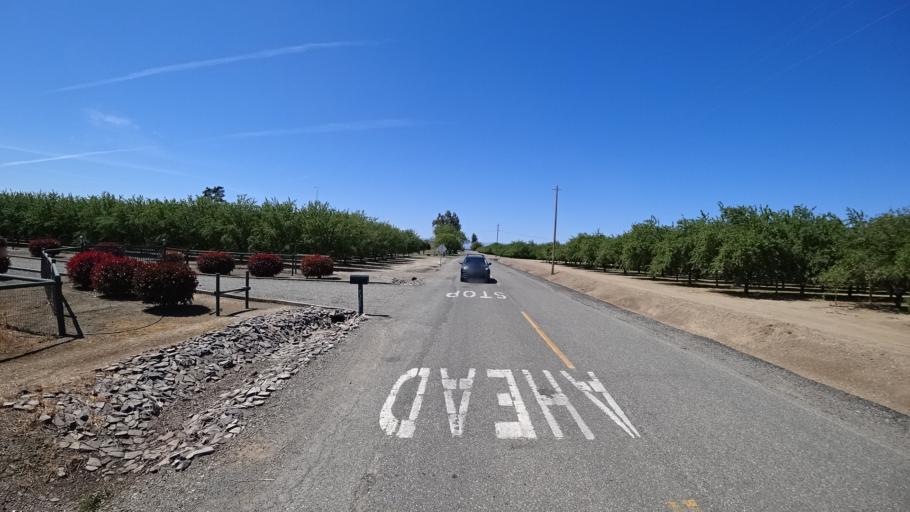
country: US
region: California
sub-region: Glenn County
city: Orland
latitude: 39.7248
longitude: -122.1065
